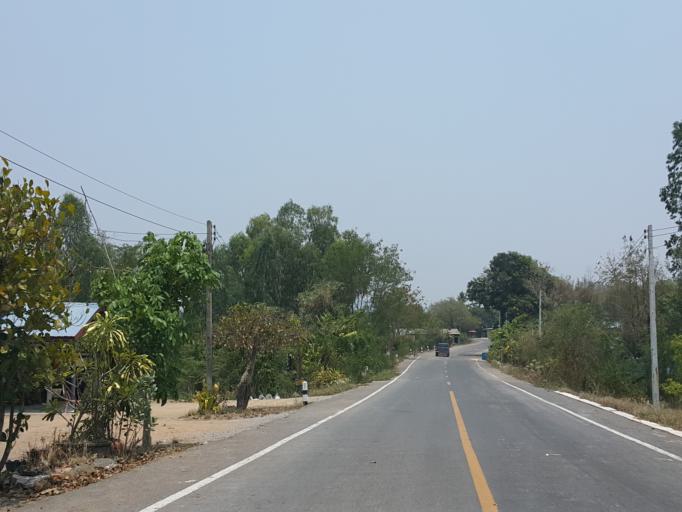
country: TH
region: Kamphaeng Phet
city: Pang Sila Thong
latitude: 16.0550
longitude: 99.3504
